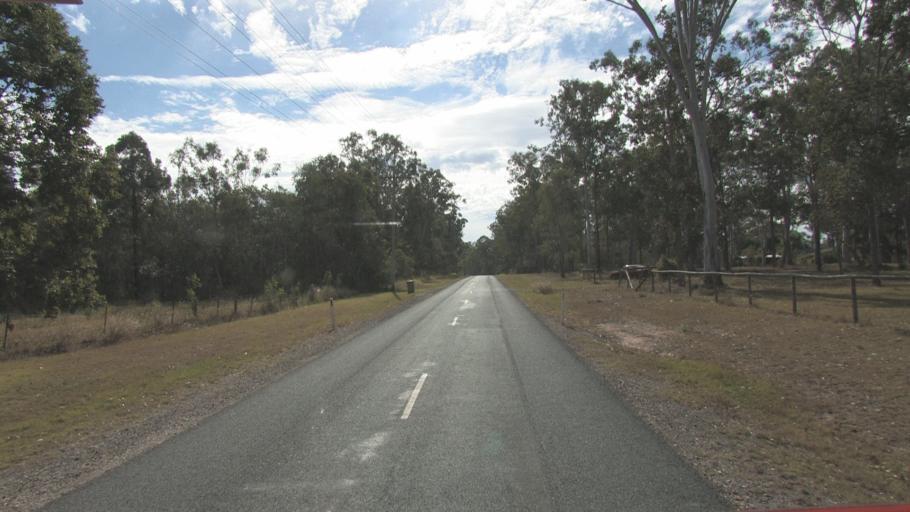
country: AU
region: Queensland
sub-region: Logan
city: North Maclean
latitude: -27.7498
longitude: 152.9735
